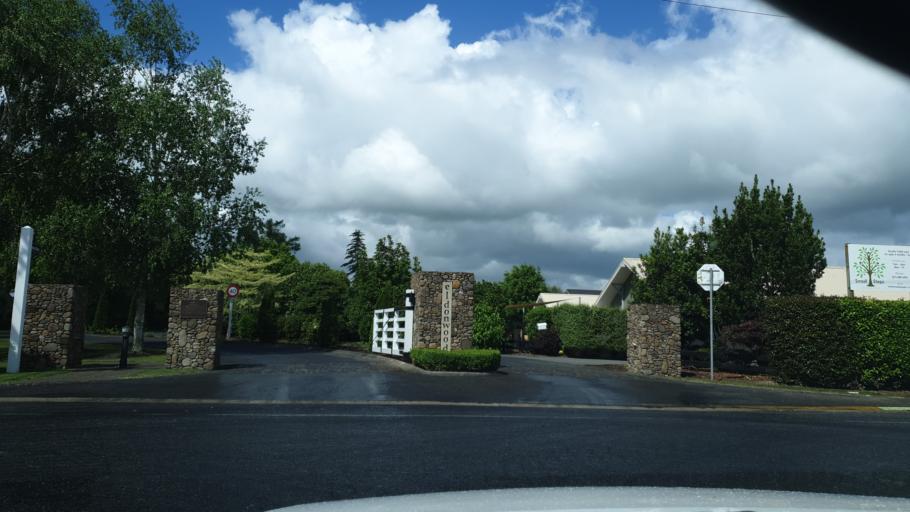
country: NZ
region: Waikato
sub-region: Matamata-Piako District
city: Matamata
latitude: -37.8174
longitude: 175.7629
